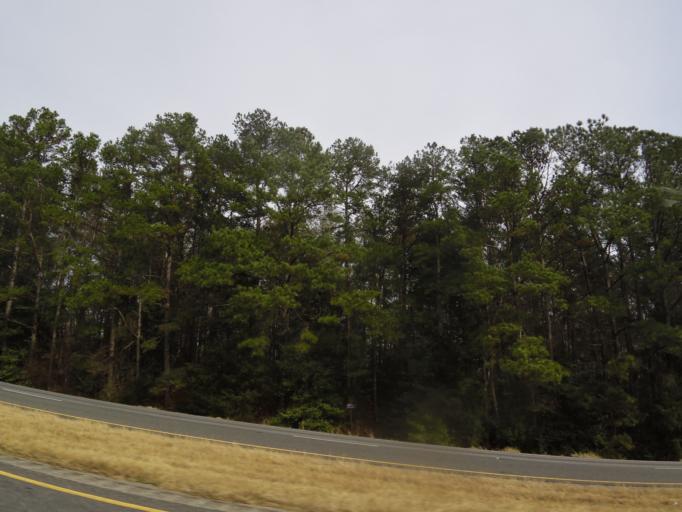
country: US
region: Alabama
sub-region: Dale County
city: Ozark
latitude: 31.5615
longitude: -85.7506
